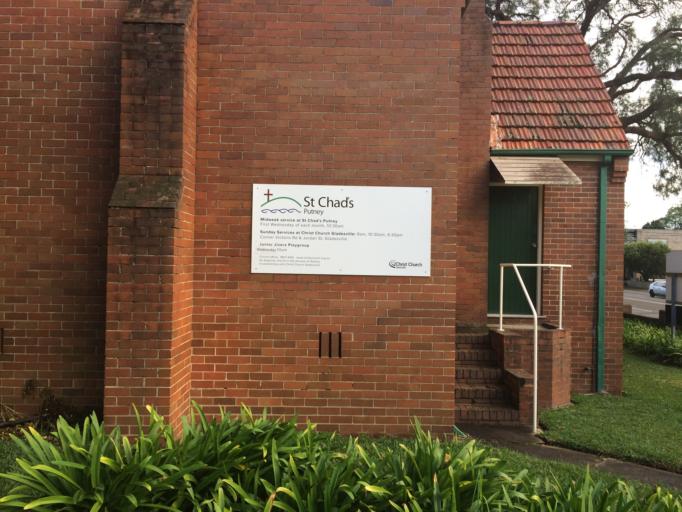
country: AU
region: New South Wales
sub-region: Canada Bay
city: Rhodes
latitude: -33.8242
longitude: 151.1090
